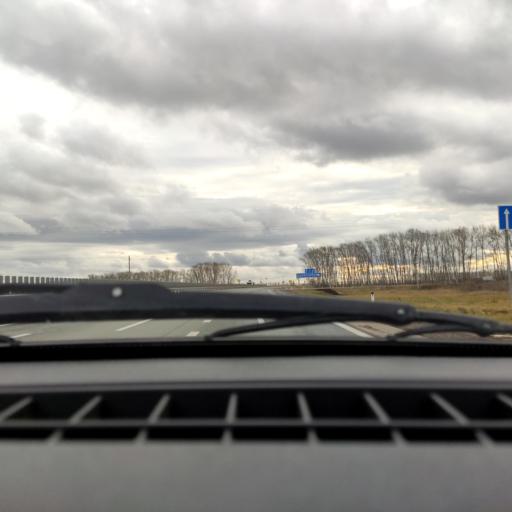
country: RU
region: Bashkortostan
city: Asanovo
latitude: 54.9625
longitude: 55.5843
